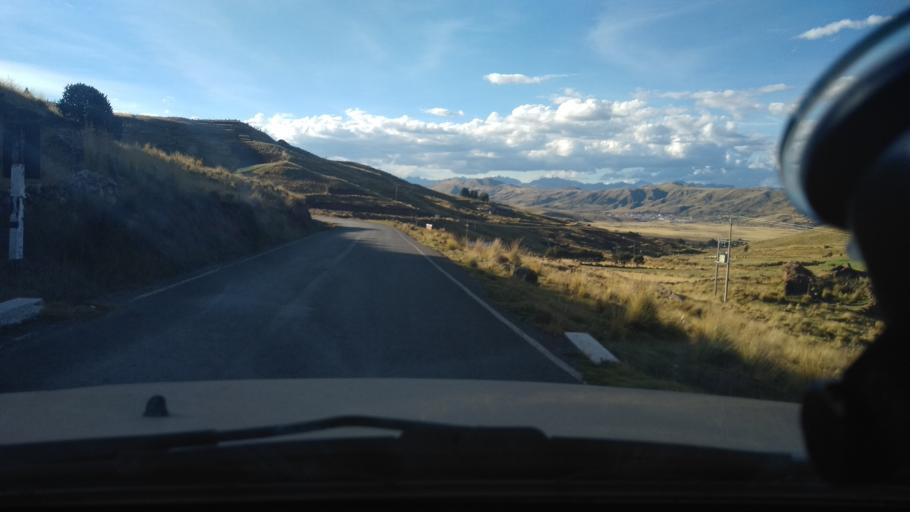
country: PE
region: Cusco
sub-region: Provincia de Canas
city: Ccaquiracunca
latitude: -14.2784
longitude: -71.4485
